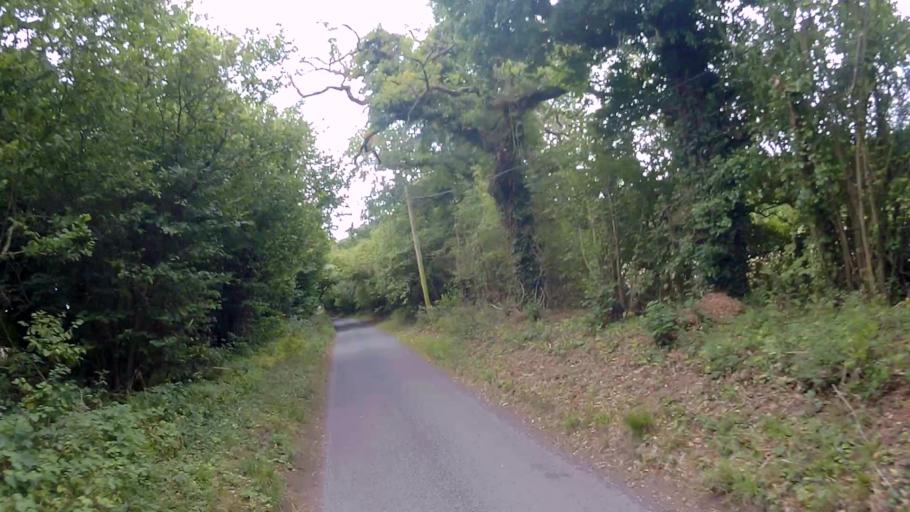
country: GB
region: England
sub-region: Hampshire
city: Overton
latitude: 51.2184
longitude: -1.2250
